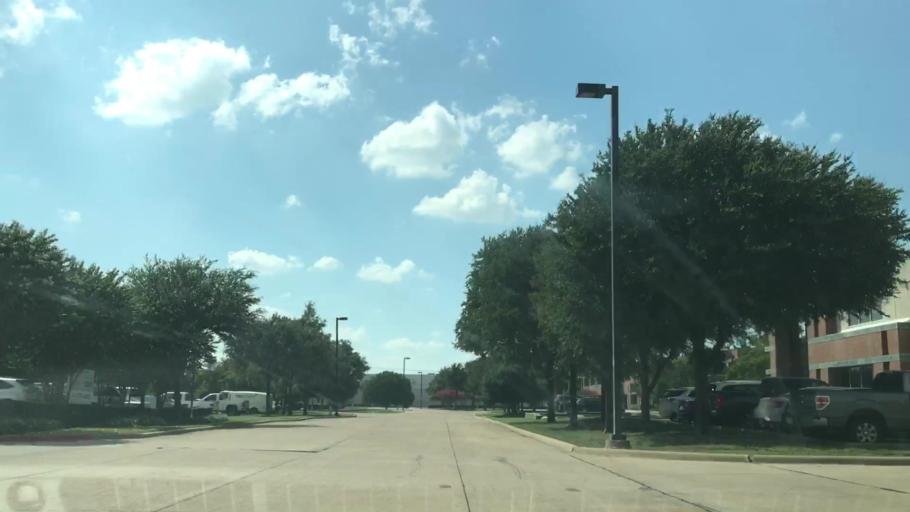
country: US
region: Texas
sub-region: Dallas County
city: Farmers Branch
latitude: 32.9431
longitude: -96.9225
